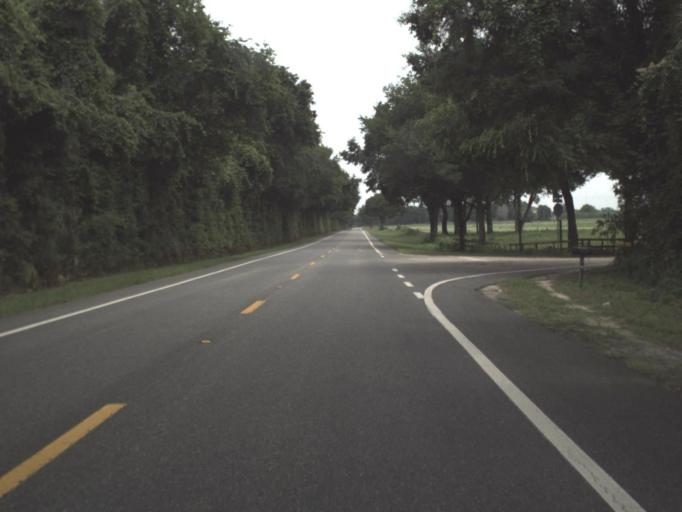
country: US
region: Florida
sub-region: Alachua County
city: Archer
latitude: 29.5764
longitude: -82.5481
